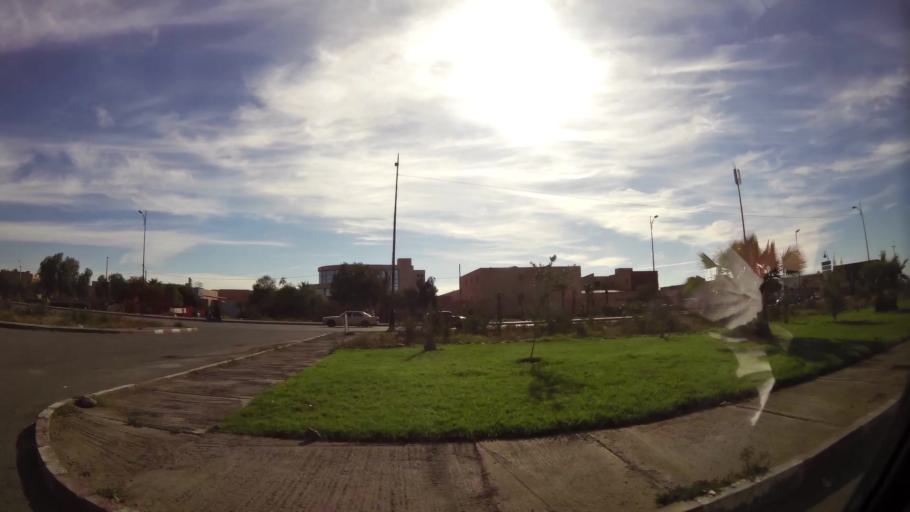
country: MA
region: Marrakech-Tensift-Al Haouz
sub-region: Marrakech
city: Marrakesh
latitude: 31.6808
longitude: -8.0487
